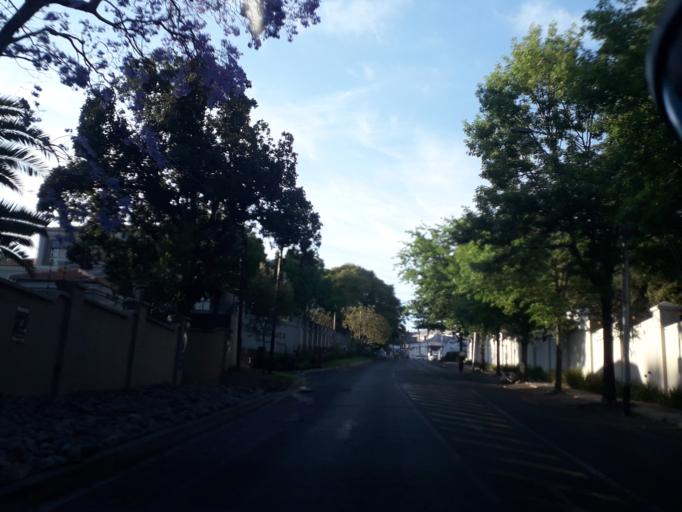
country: ZA
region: Gauteng
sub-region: City of Johannesburg Metropolitan Municipality
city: Johannesburg
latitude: -26.1201
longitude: 28.0300
